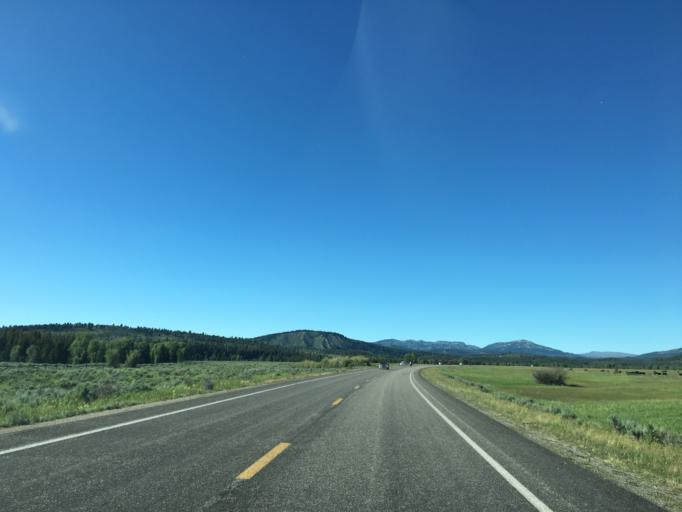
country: US
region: Wyoming
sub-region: Teton County
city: Jackson
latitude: 43.8140
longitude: -110.5261
